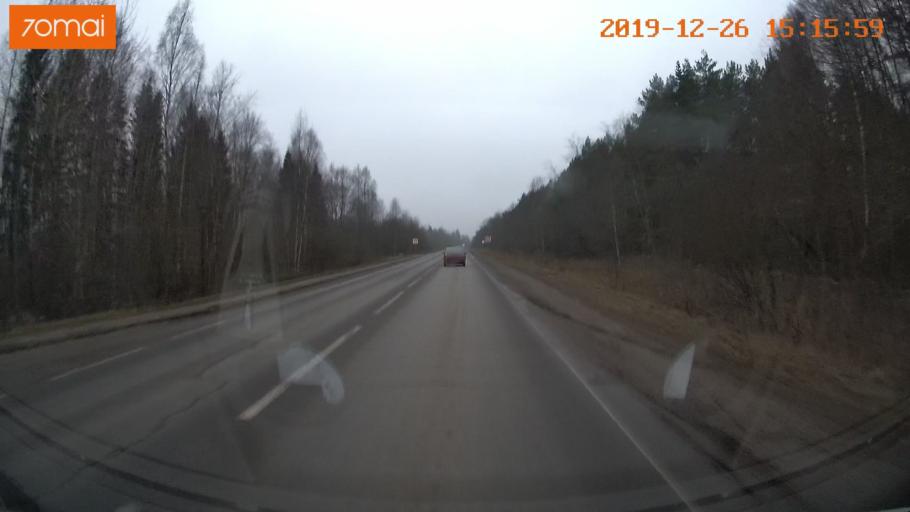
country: RU
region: Jaroslavl
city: Rybinsk
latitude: 58.0912
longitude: 38.8718
